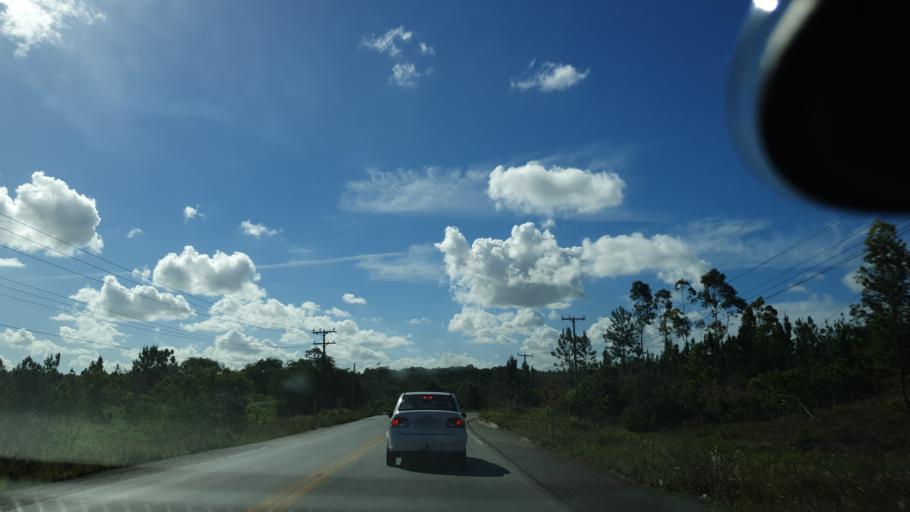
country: BR
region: Bahia
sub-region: Camacari
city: Camacari
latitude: -12.6837
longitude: -38.2791
